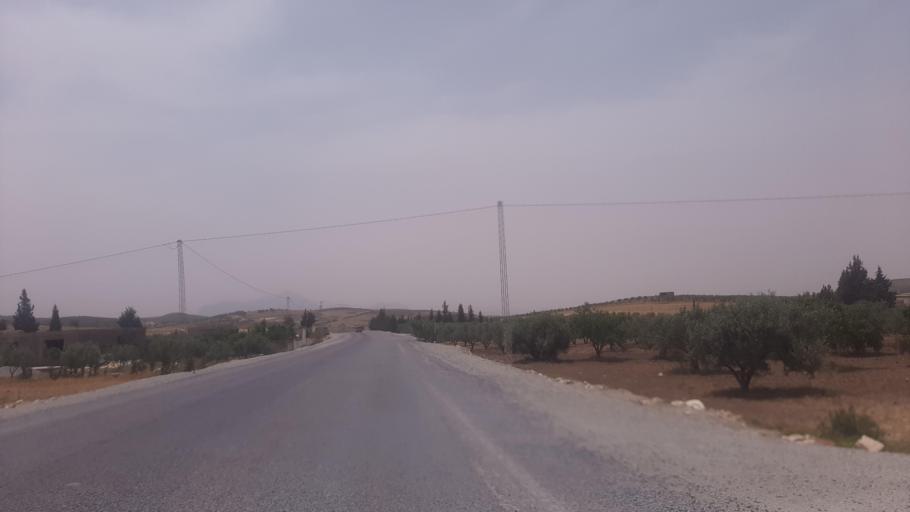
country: TN
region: Zaghwan
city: Zaghouan
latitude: 36.5207
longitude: 10.1583
